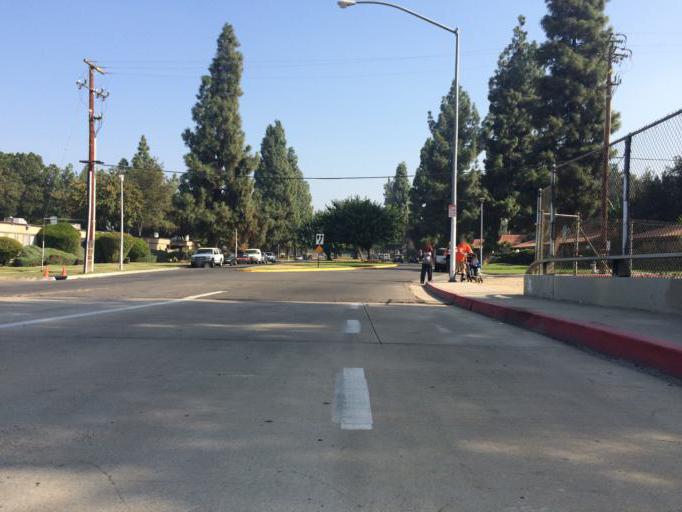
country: US
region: California
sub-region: Fresno County
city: Fresno
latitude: 36.7395
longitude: -119.7773
